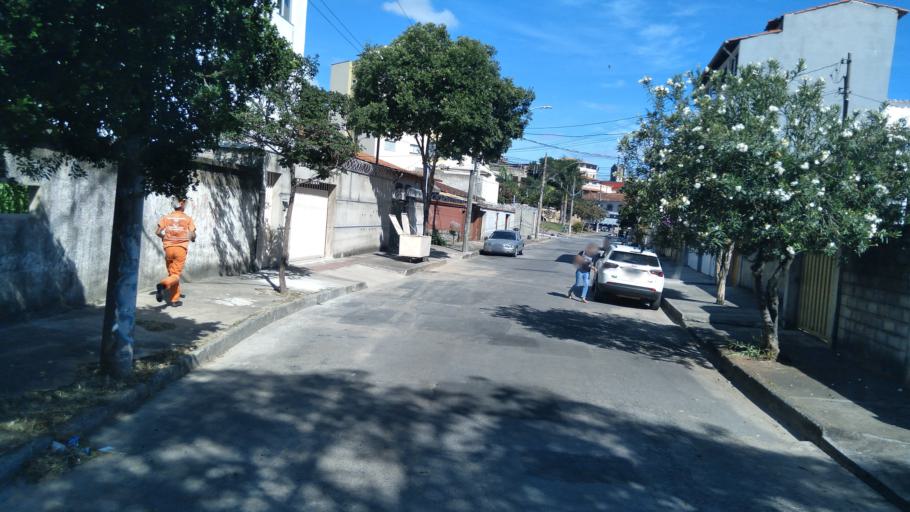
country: BR
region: Minas Gerais
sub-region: Belo Horizonte
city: Belo Horizonte
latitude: -19.8563
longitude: -43.9132
